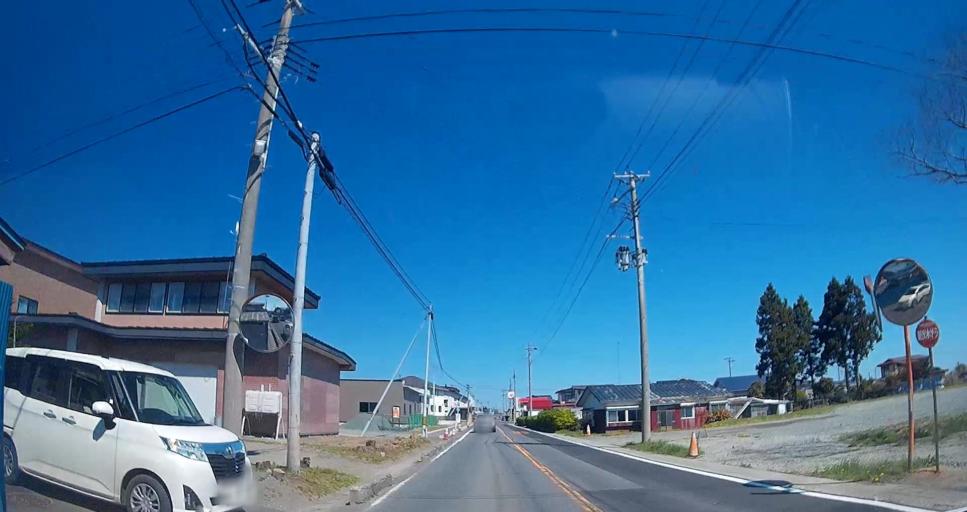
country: JP
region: Aomori
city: Misawa
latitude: 40.6583
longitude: 141.4354
